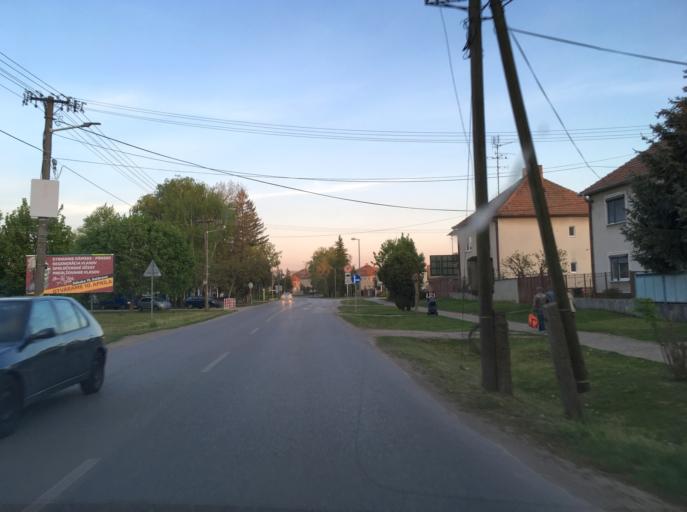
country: SK
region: Nitriansky
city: Kolarovo
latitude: 47.9155
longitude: 17.9984
